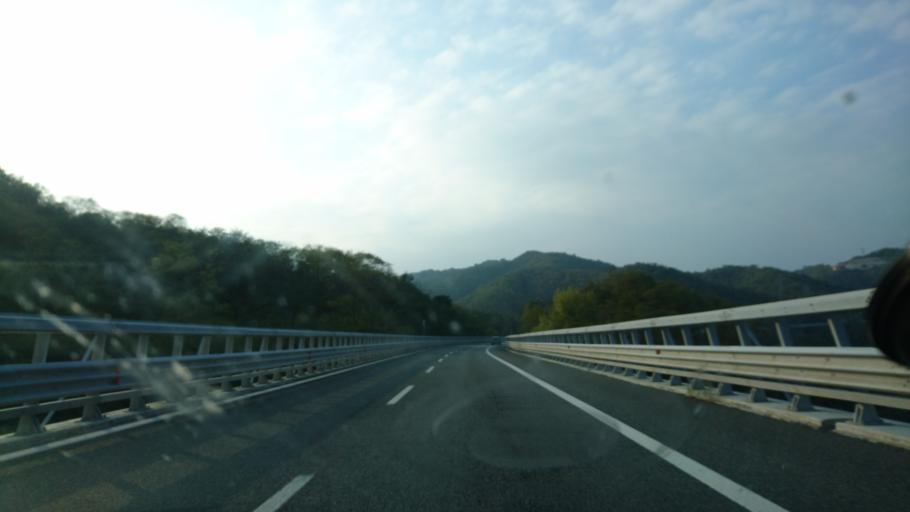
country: IT
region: Liguria
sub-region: Provincia di Savona
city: Altare
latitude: 44.3246
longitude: 8.3725
